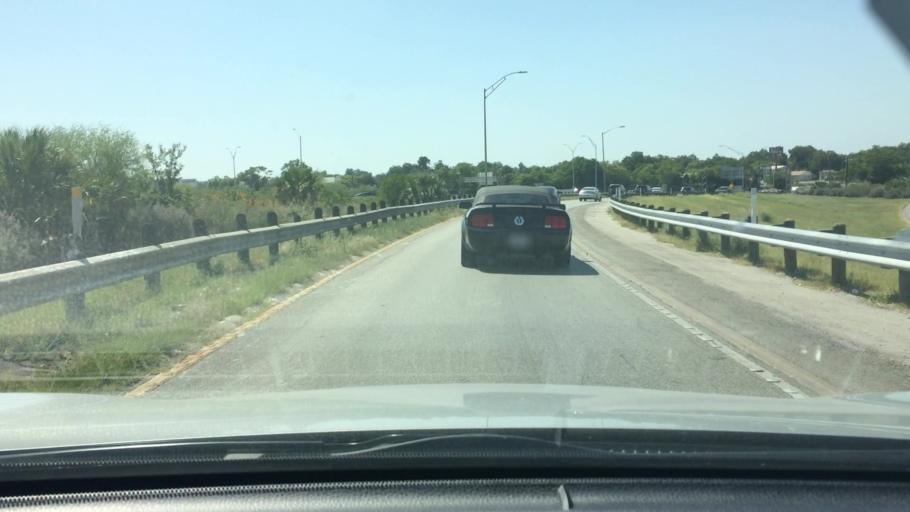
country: US
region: Texas
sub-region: Bexar County
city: San Antonio
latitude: 29.3969
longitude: -98.5096
